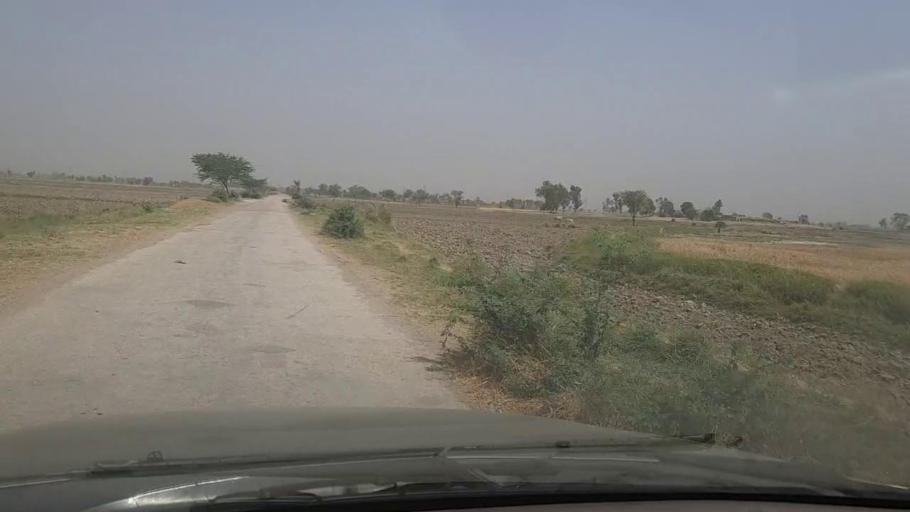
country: PK
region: Sindh
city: Madeji
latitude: 27.8173
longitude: 68.3977
